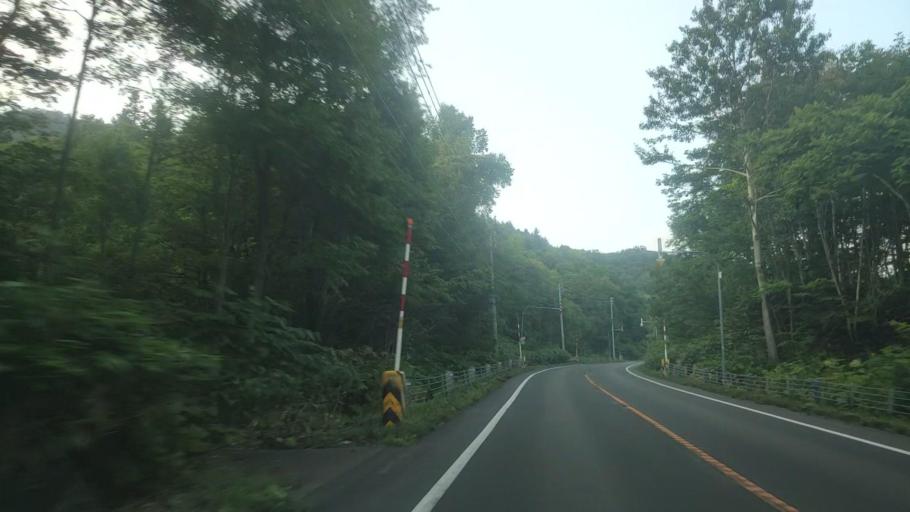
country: JP
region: Hokkaido
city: Bibai
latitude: 43.2649
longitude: 142.0319
